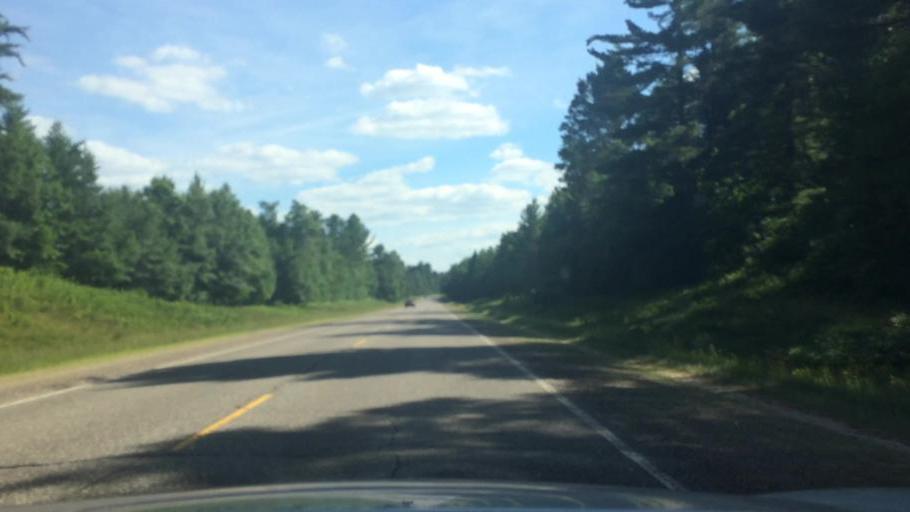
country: US
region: Wisconsin
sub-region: Vilas County
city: Lac du Flambeau
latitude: 46.0700
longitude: -89.6445
